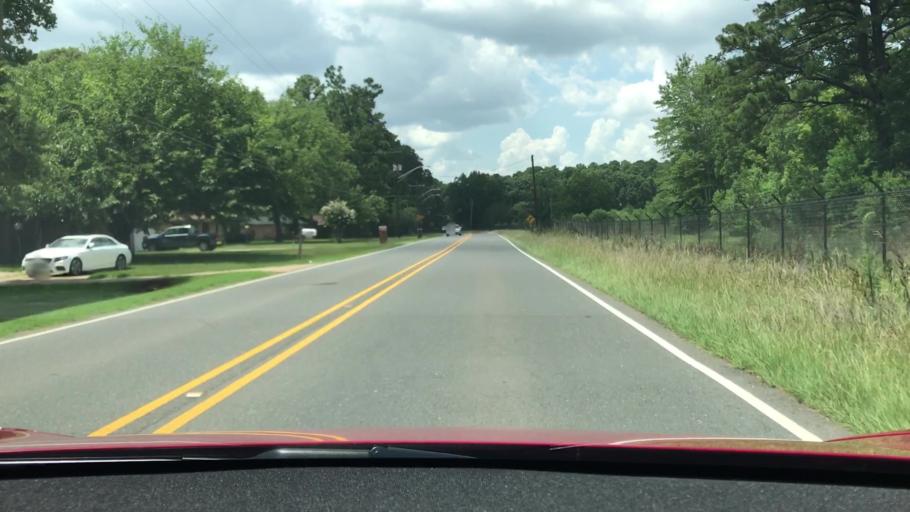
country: US
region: Louisiana
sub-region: Bossier Parish
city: Bossier City
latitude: 32.3890
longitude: -93.7205
